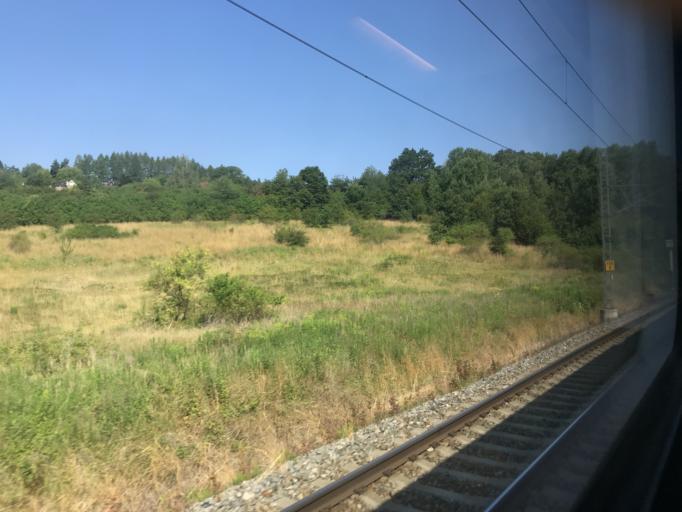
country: CZ
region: Central Bohemia
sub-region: Okres Praha-Vychod
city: Mnichovice
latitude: 49.9404
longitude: 14.6998
